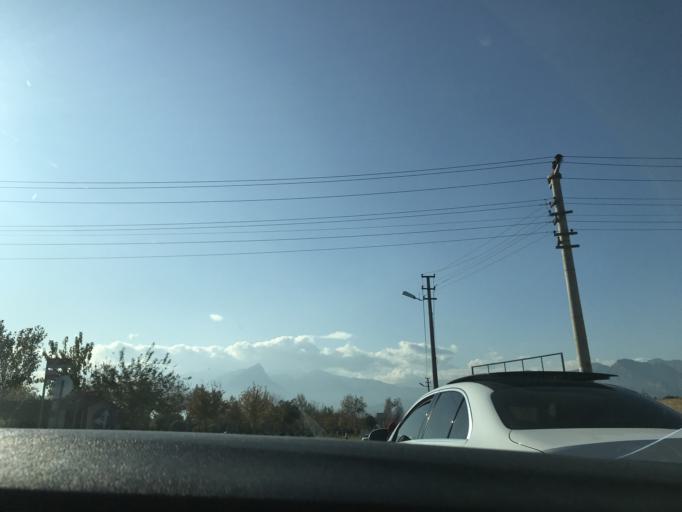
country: TR
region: Antalya
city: Antalya
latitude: 36.9022
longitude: 30.6521
